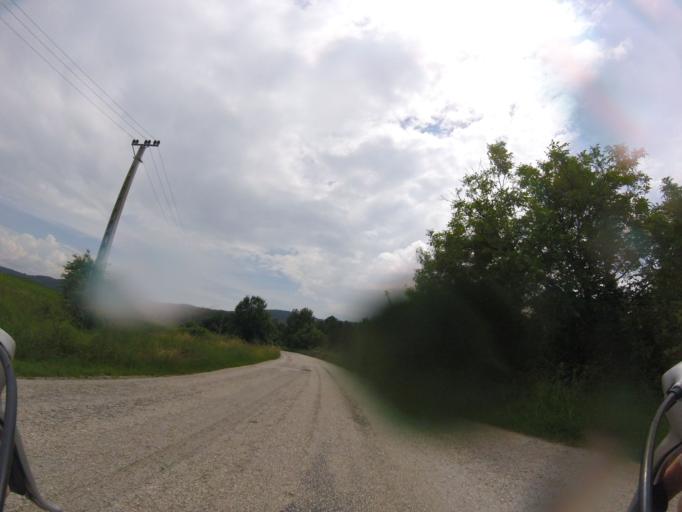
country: HU
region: Baranya
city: Villany
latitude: 45.8935
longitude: 18.4027
